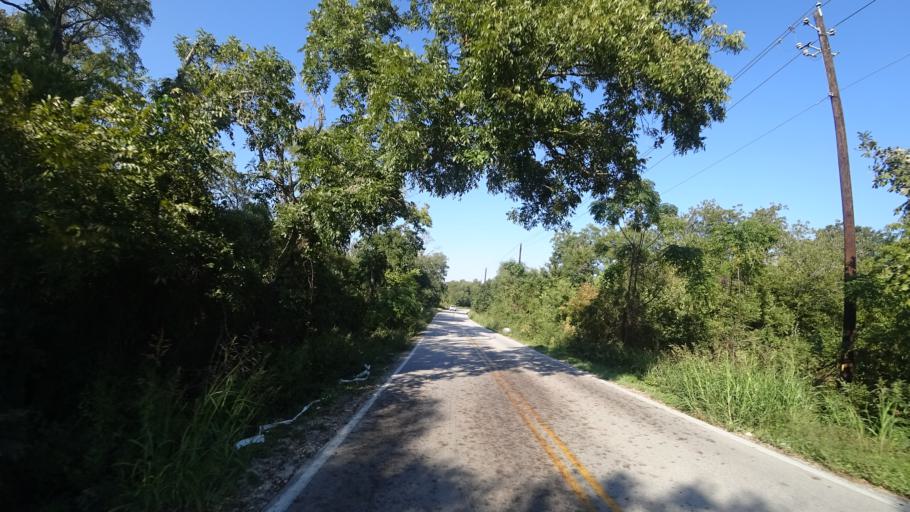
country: US
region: Texas
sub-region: Travis County
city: Pflugerville
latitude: 30.3513
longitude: -97.6548
